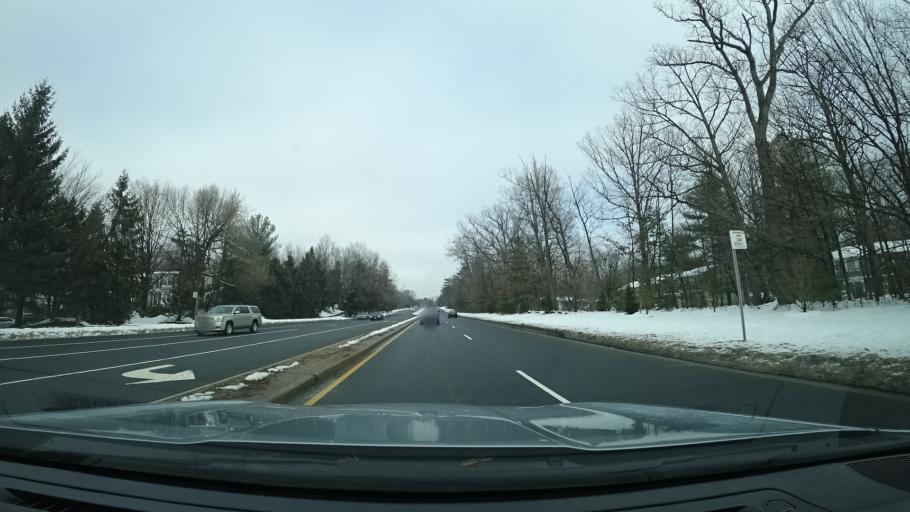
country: US
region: Virginia
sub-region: Fairfax County
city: Reston
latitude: 38.9738
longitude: -77.3515
